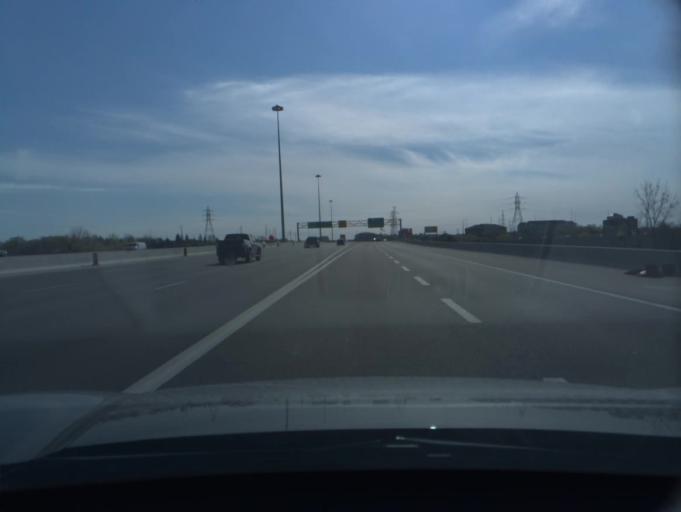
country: CA
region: Ontario
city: North Perth
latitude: 43.8269
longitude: -80.9999
